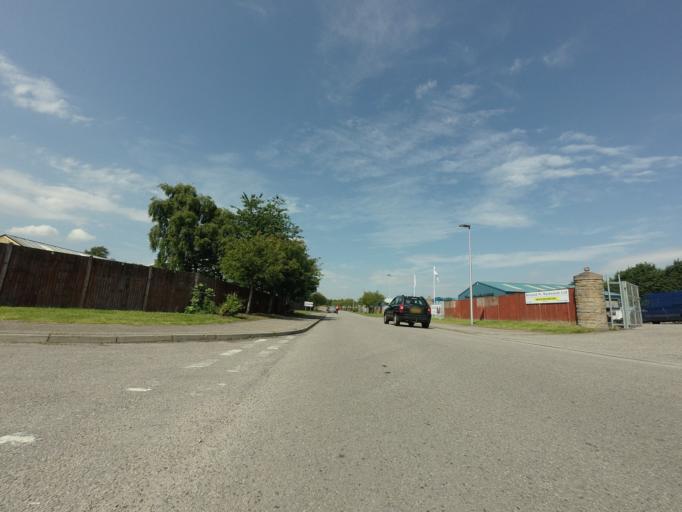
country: GB
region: Scotland
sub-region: Highland
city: Tain
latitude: 57.8164
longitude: -4.0592
